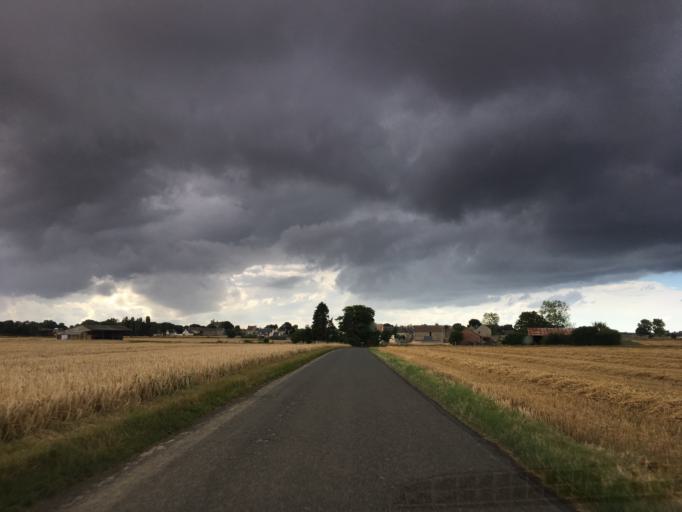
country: FR
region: Lower Normandy
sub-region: Departement du Calvados
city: Luc-sur-Mer
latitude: 49.3070
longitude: -0.3446
